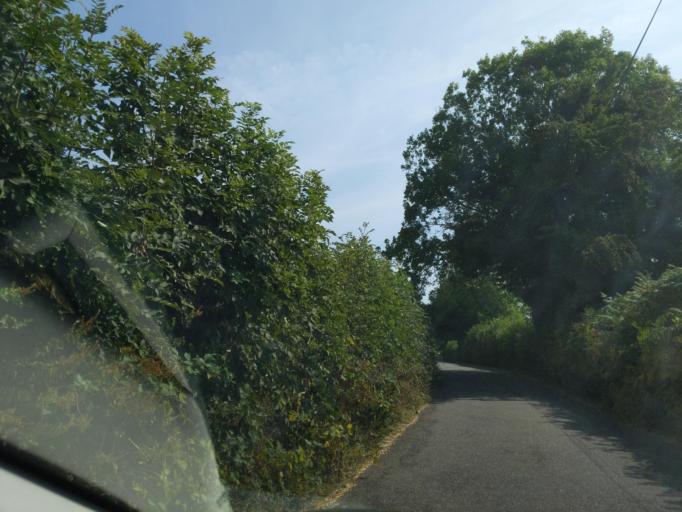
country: GB
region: England
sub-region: Devon
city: Winkleigh
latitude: 50.8839
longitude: -3.8731
